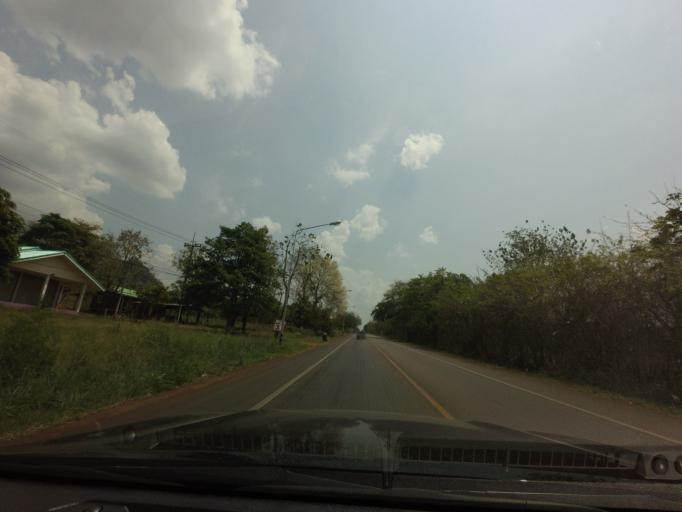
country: TH
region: Kanchanaburi
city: Sai Yok
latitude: 14.1339
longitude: 99.1565
